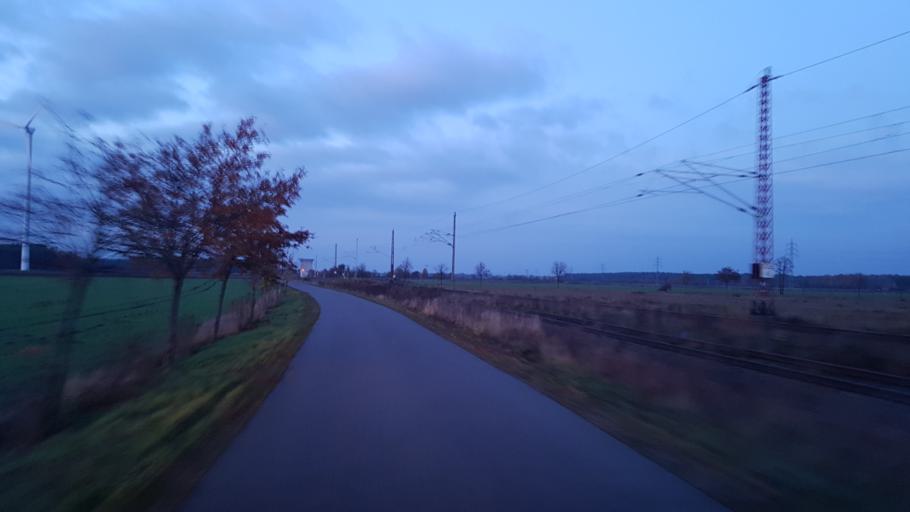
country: DE
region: Brandenburg
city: Falkenberg
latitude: 51.6319
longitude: 13.2250
